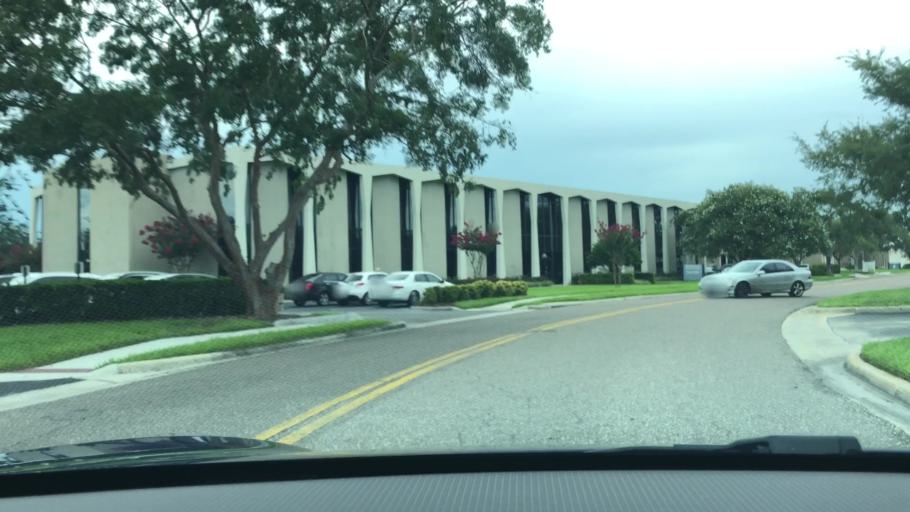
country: US
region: Florida
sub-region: Orange County
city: Orlando
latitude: 28.5570
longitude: -81.3438
